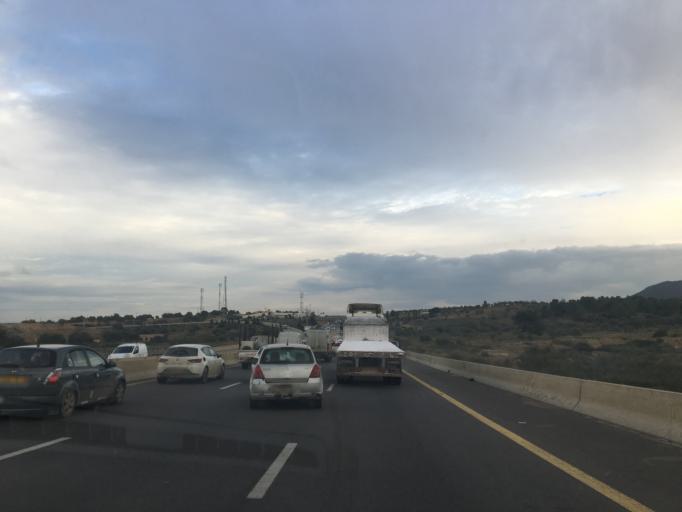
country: DZ
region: Bouira
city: Chorfa
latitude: 36.3168
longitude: 4.1510
